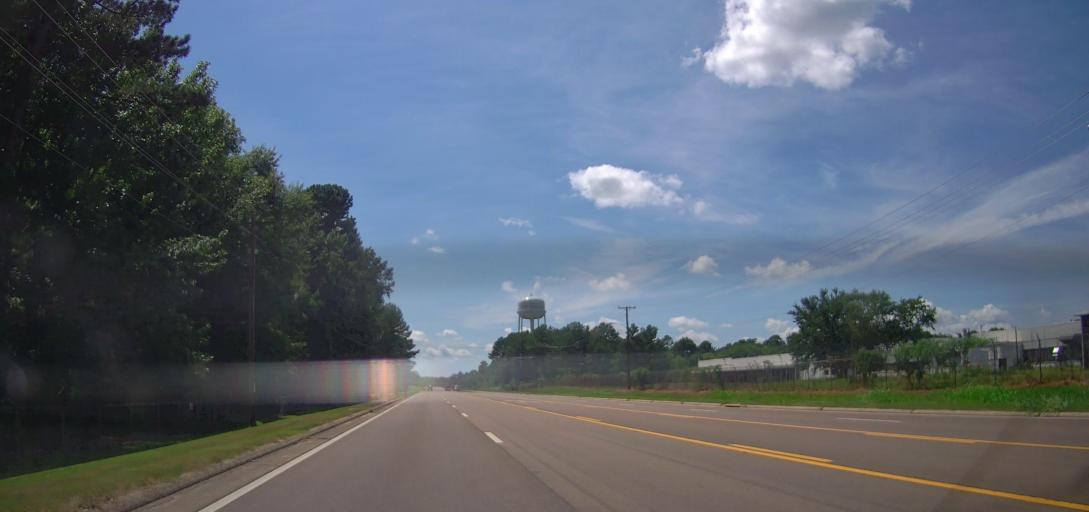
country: US
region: Mississippi
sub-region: Monroe County
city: Aberdeen
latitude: 33.8149
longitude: -88.5545
